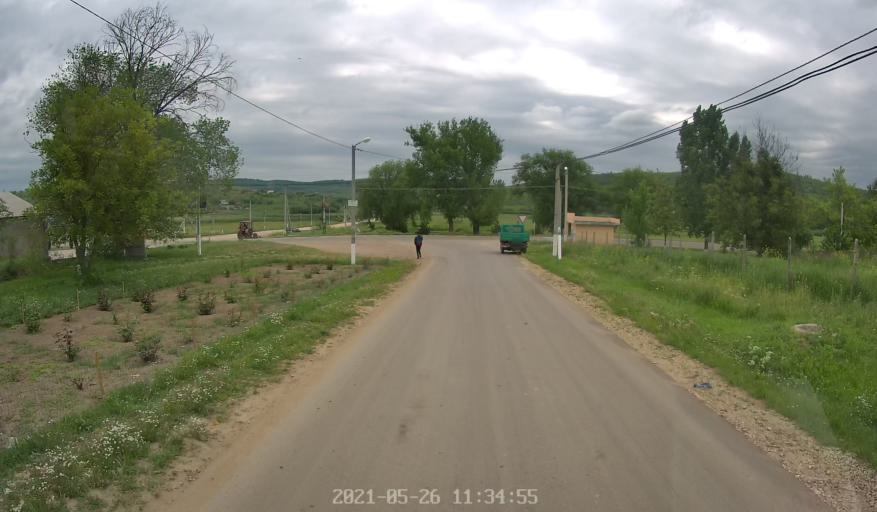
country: MD
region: Hincesti
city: Dancu
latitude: 46.8252
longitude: 28.3686
